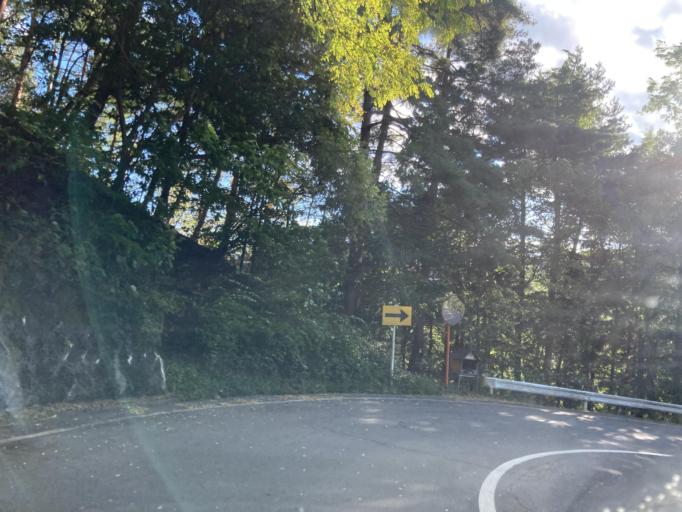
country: JP
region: Nagano
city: Ueda
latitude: 36.4023
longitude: 138.1027
